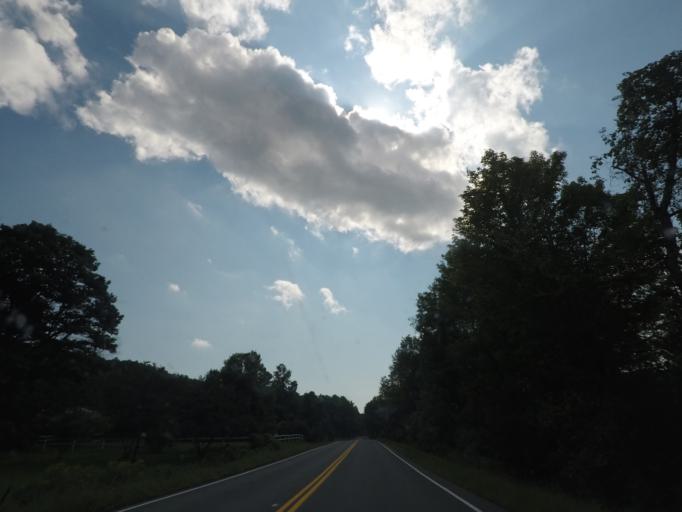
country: US
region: New York
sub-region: Rensselaer County
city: Poestenkill
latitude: 42.7763
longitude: -73.5376
